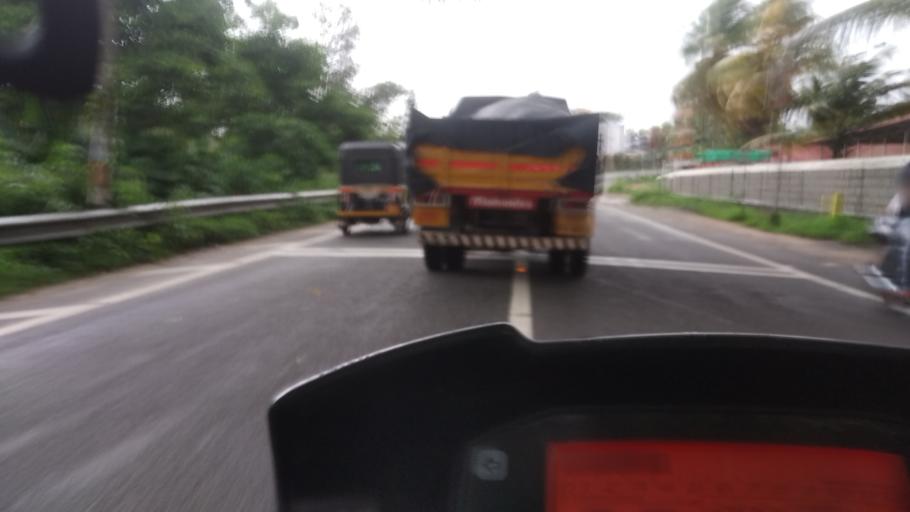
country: IN
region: Kerala
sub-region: Thiruvananthapuram
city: Attingal
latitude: 8.7106
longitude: 76.8124
